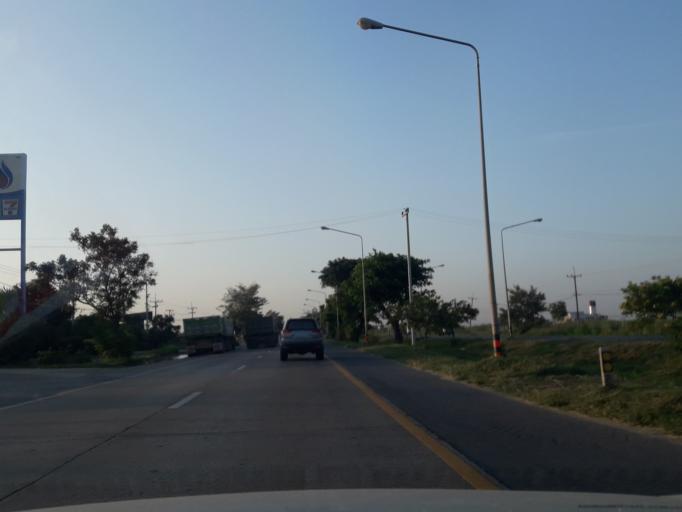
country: TH
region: Phra Nakhon Si Ayutthaya
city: Phra Nakhon Si Ayutthaya
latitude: 14.3380
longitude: 100.5281
